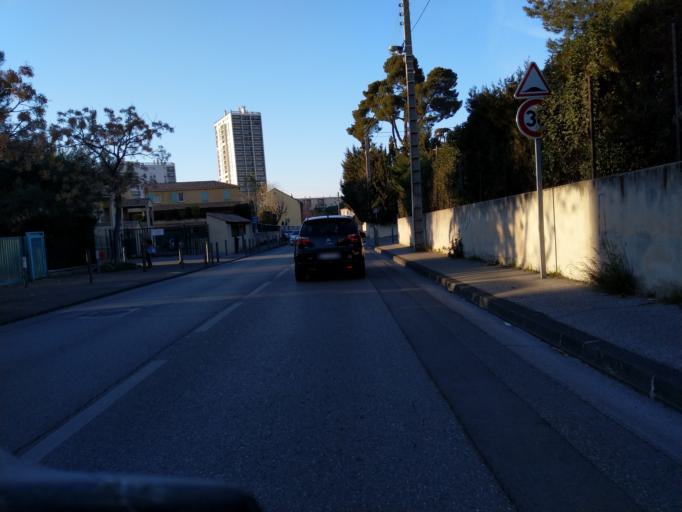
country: FR
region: Provence-Alpes-Cote d'Azur
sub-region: Departement des Bouches-du-Rhone
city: Marseille 10
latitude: 43.2774
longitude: 5.4304
